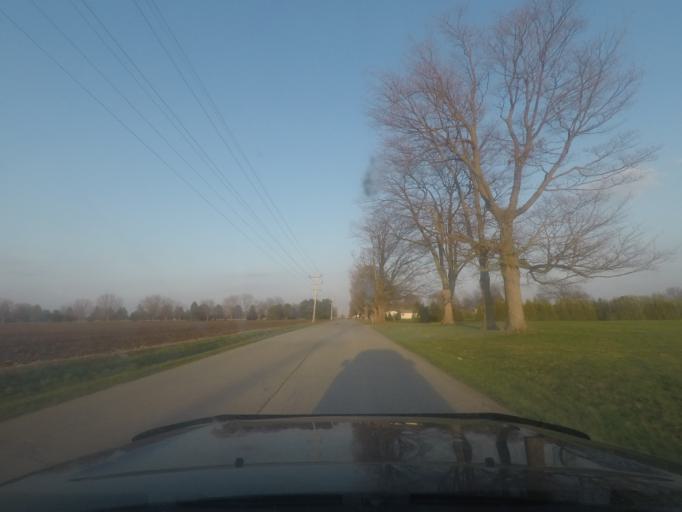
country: US
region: Indiana
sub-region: LaPorte County
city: LaPorte
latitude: 41.5692
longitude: -86.7181
